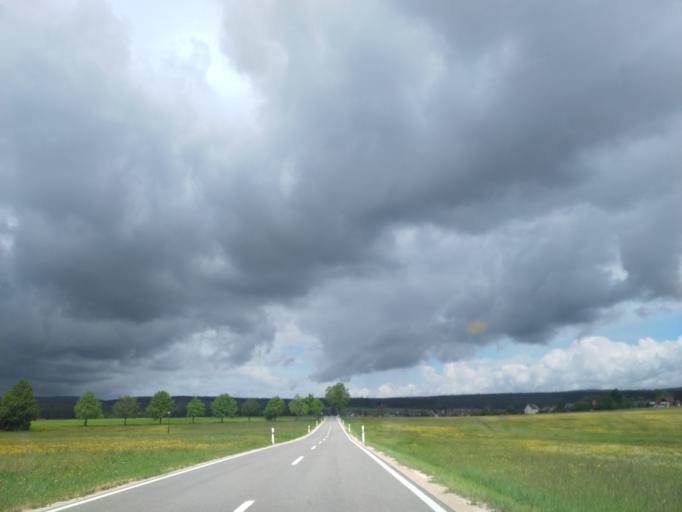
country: DE
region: Baden-Wuerttemberg
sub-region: Freiburg Region
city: Loffingen
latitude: 47.8848
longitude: 8.3038
